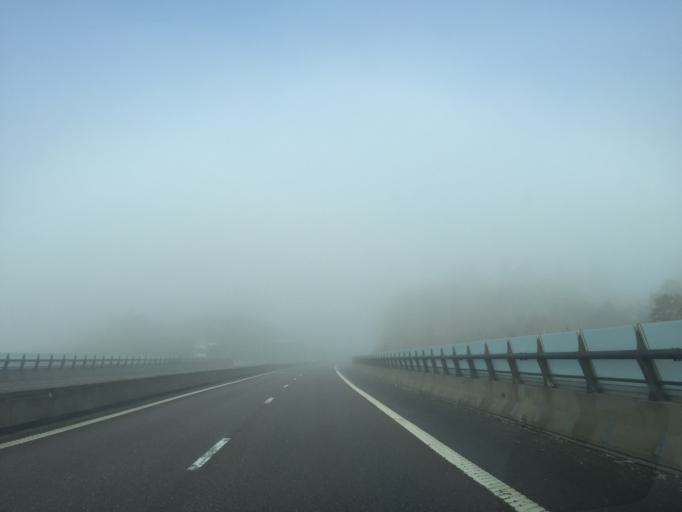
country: SE
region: Vaestra Goetaland
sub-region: Uddevalla Kommun
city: Uddevalla
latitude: 58.3298
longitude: 11.8360
